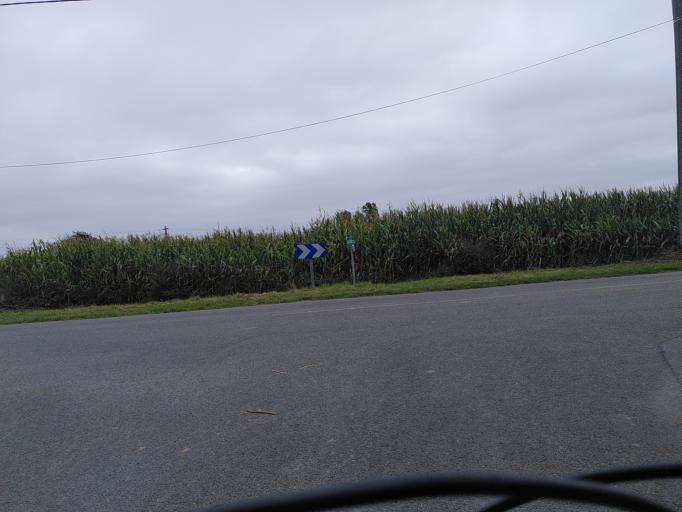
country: FR
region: Nord-Pas-de-Calais
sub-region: Departement du Nord
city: Bois-Grenier
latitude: 50.6306
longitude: 2.8585
